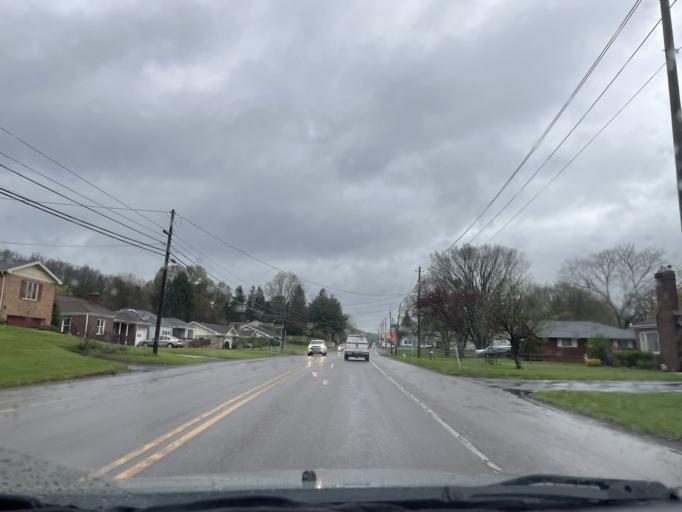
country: US
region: Maryland
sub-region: Garrett County
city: Oakland
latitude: 39.4154
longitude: -79.4028
